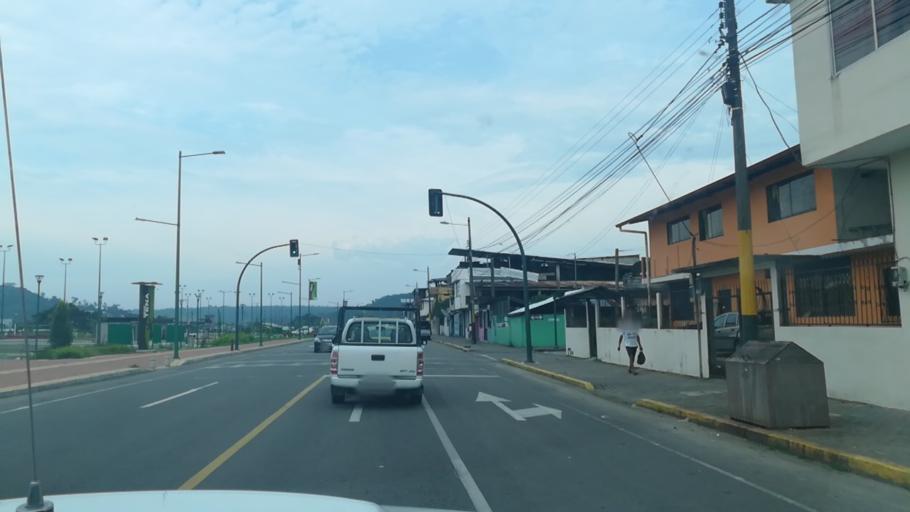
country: EC
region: Napo
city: Tena
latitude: -0.9869
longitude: -77.8204
